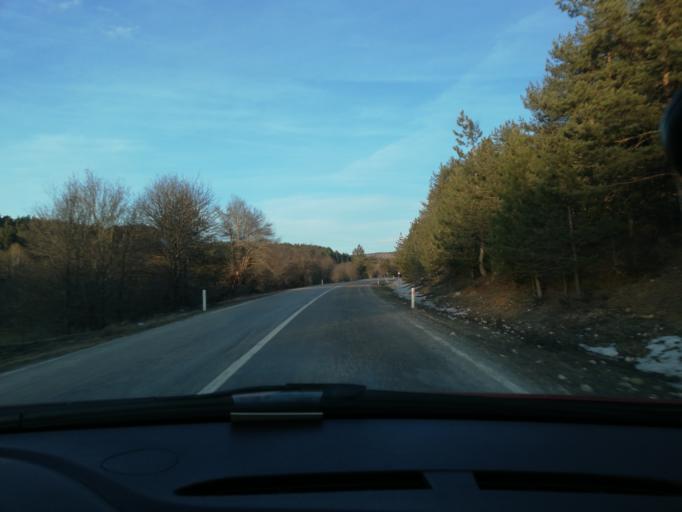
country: TR
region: Kastamonu
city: Agli
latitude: 41.6988
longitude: 33.6342
